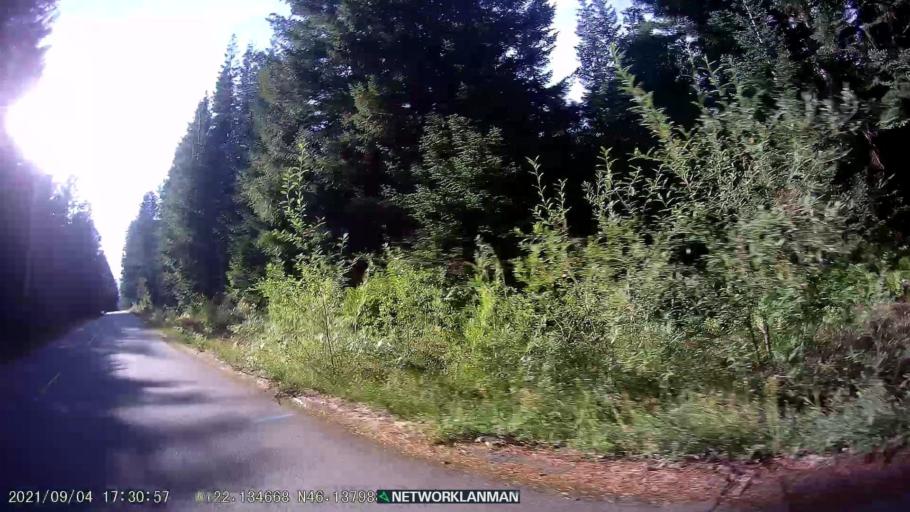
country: US
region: Washington
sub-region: Clark County
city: Yacolt
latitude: 46.1380
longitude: -122.1348
